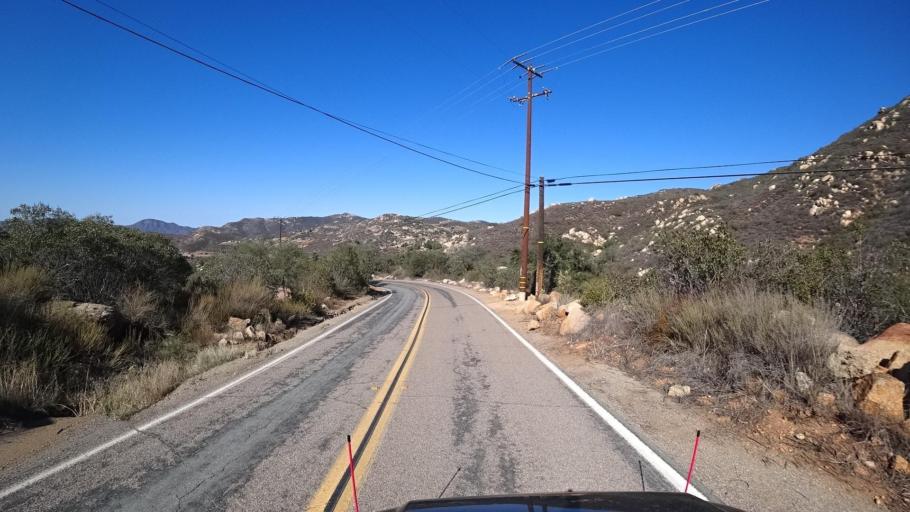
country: US
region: California
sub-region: San Diego County
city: Jamul
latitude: 32.7087
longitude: -116.7886
